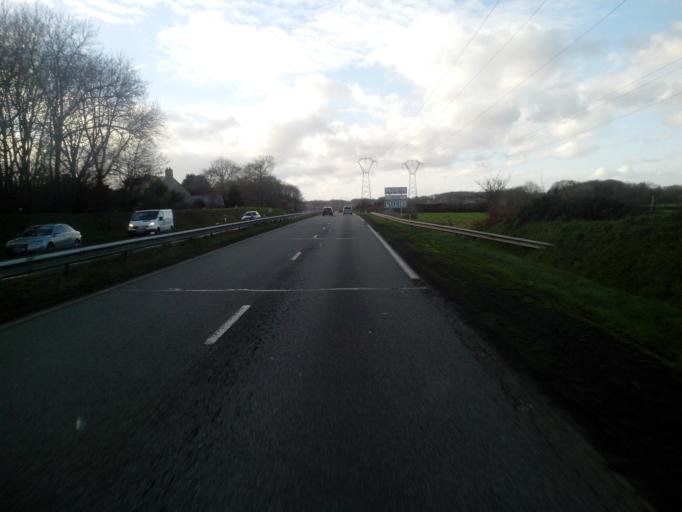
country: FR
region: Brittany
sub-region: Departement des Cotes-d'Armor
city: Plouer-sur-Rance
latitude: 48.5368
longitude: -1.9835
